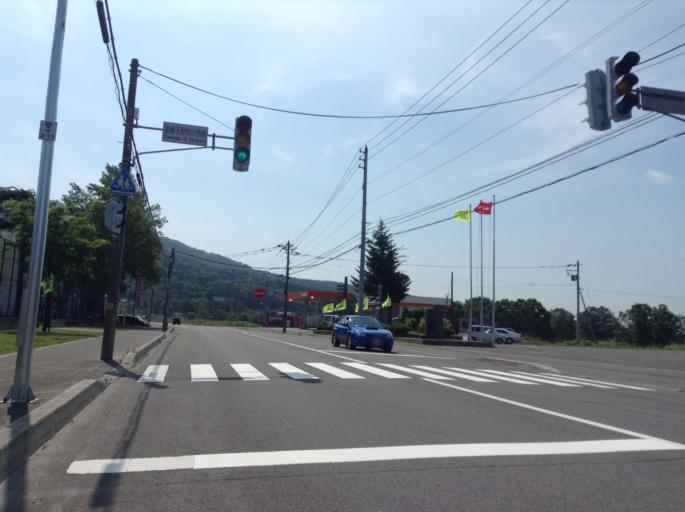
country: JP
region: Hokkaido
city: Nayoro
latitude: 44.7258
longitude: 142.2627
